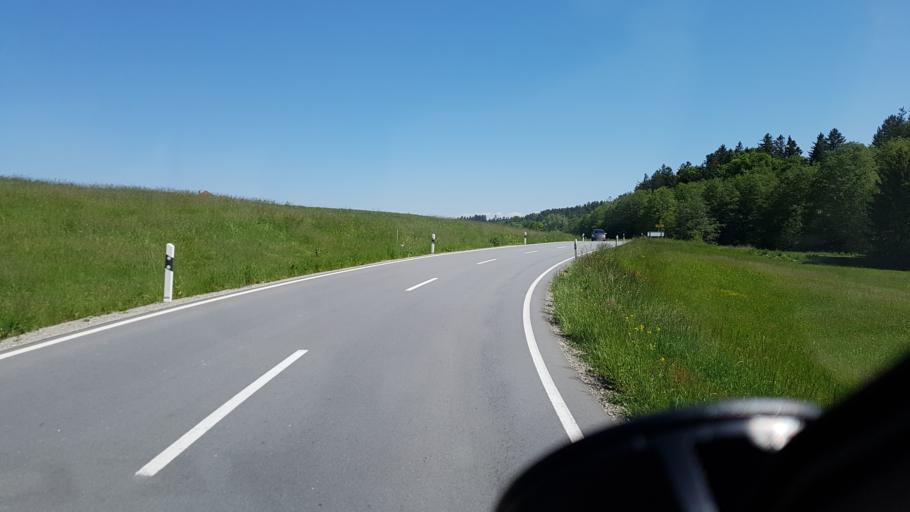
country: DE
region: Bavaria
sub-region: Lower Bavaria
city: Tann
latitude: 48.3486
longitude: 12.8841
